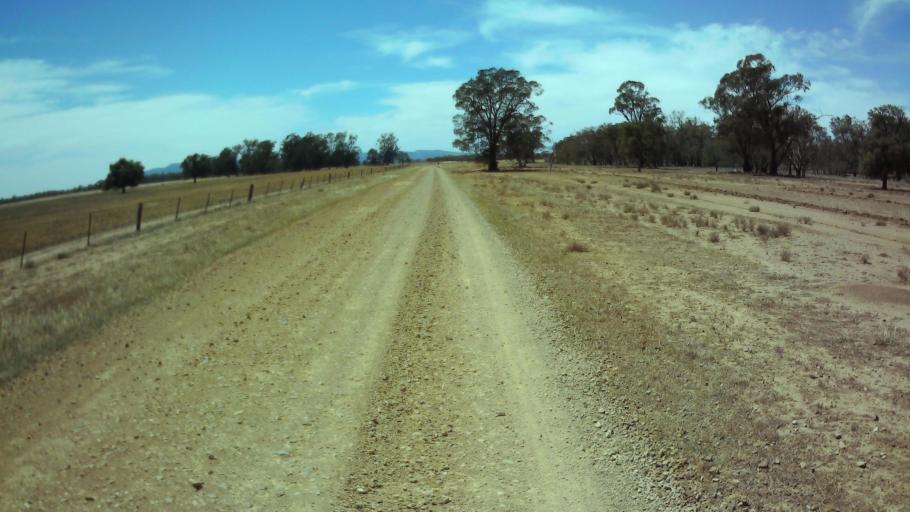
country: AU
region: New South Wales
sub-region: Weddin
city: Grenfell
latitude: -33.8614
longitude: 147.7559
